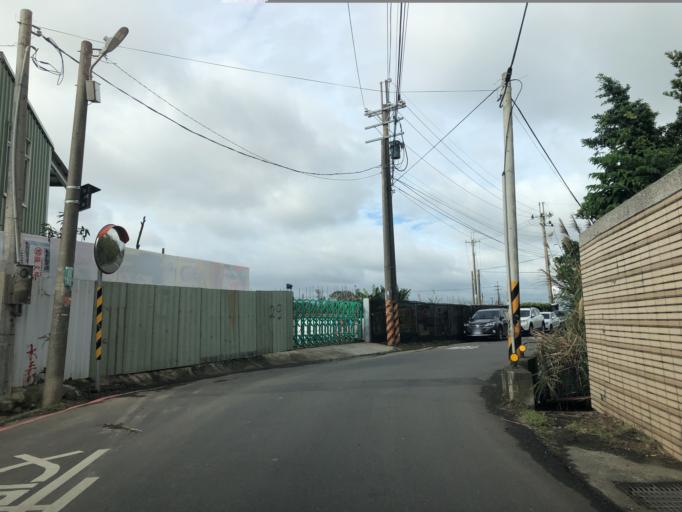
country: TW
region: Taiwan
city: Daxi
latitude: 24.9177
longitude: 121.2591
